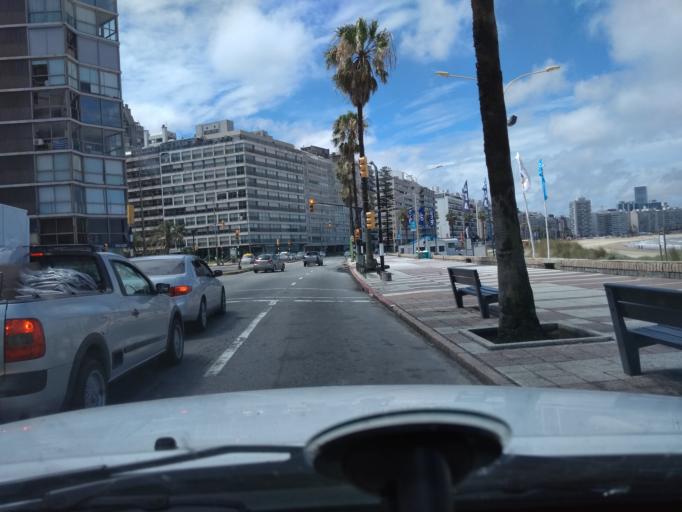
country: UY
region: Montevideo
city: Montevideo
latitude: -34.9156
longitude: -56.1488
